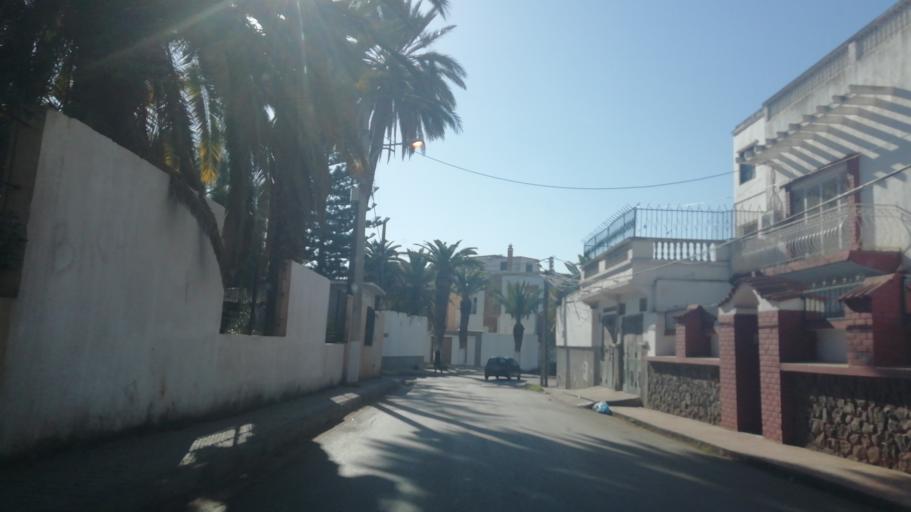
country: DZ
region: Oran
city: Oran
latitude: 35.6755
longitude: -0.6447
